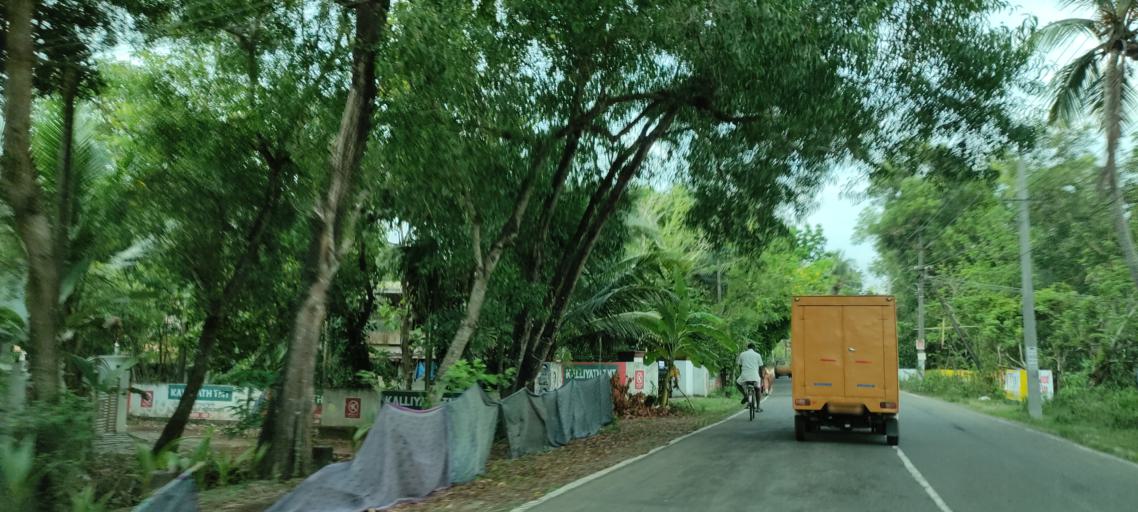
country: IN
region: Kerala
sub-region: Kottayam
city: Vaikam
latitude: 9.7622
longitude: 76.3628
